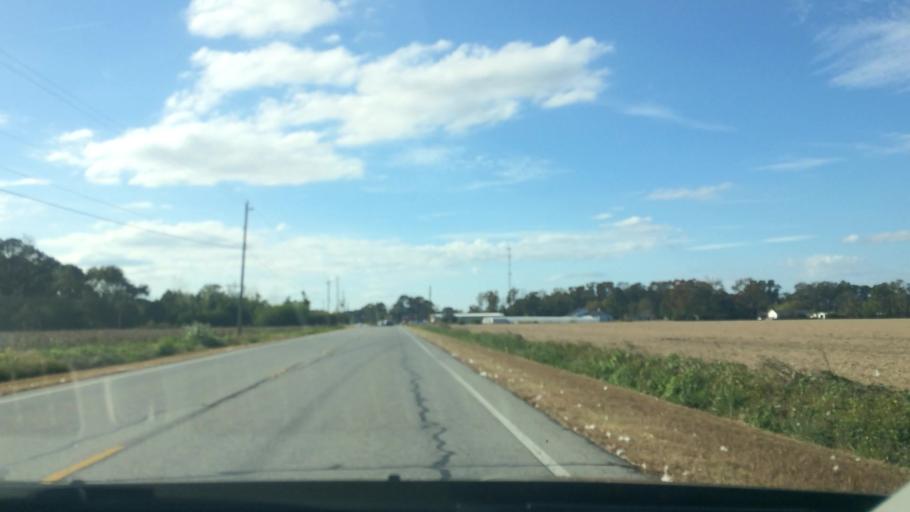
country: US
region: North Carolina
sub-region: Greene County
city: Snow Hill
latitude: 35.4394
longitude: -77.7860
